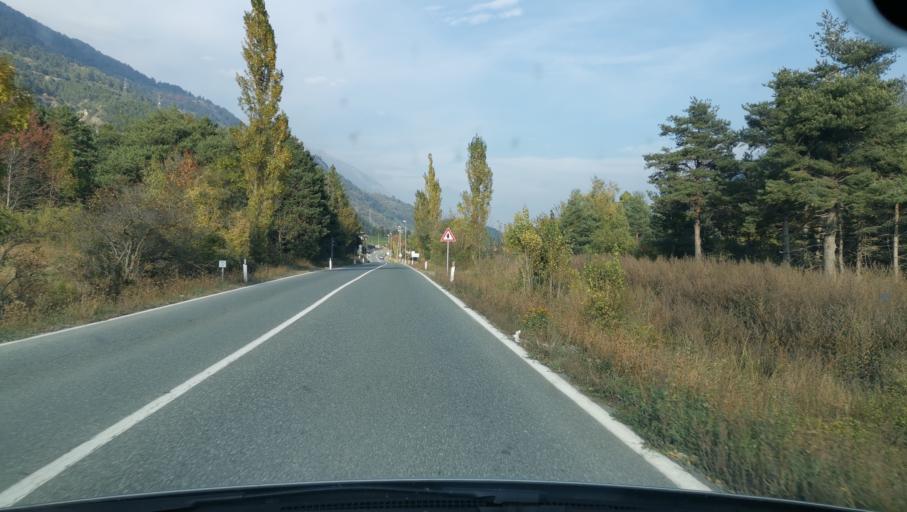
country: IT
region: Piedmont
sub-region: Provincia di Torino
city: Salbertrand
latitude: 45.0662
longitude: 6.8752
